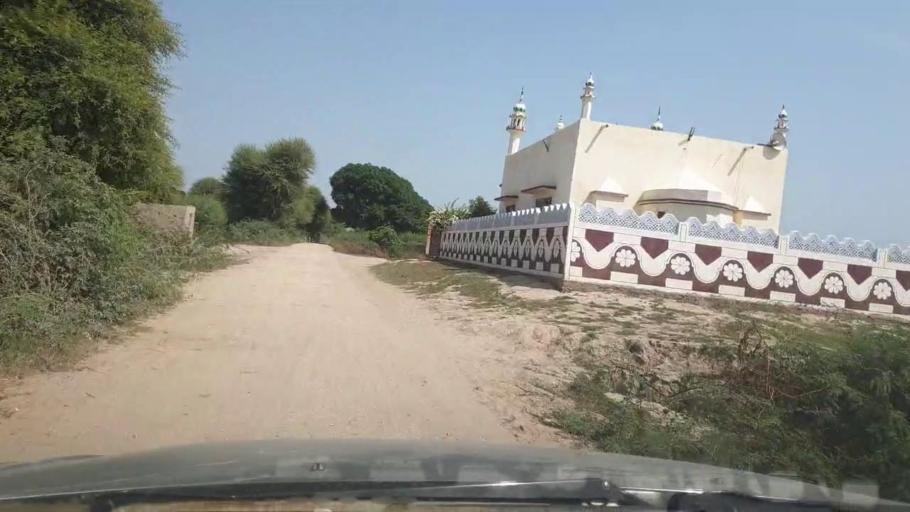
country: PK
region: Sindh
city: Tando Ghulam Ali
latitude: 25.1589
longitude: 68.8857
